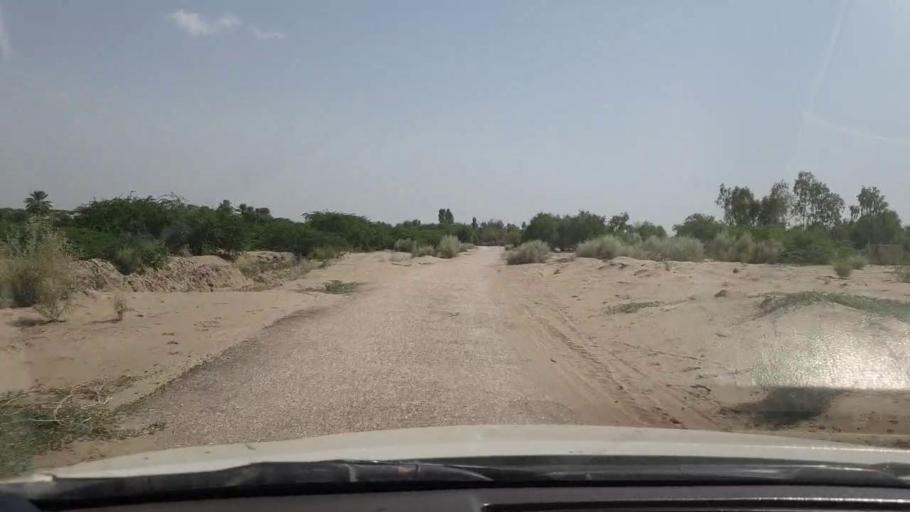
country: PK
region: Sindh
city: Rohri
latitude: 27.4656
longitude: 69.0789
